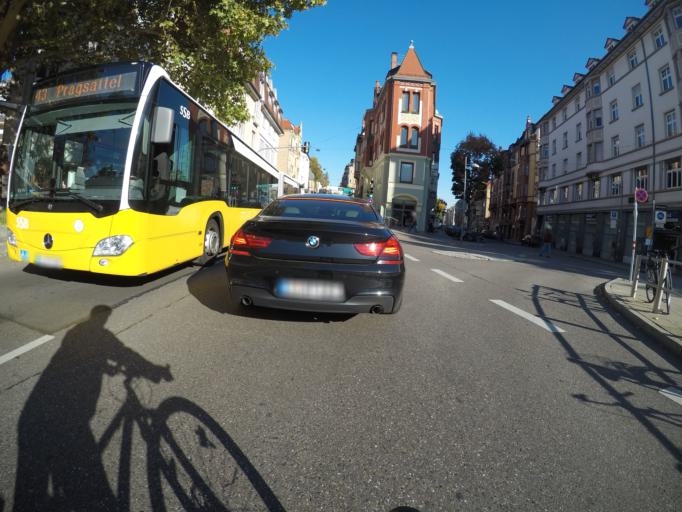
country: DE
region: Baden-Wuerttemberg
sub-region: Regierungsbezirk Stuttgart
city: Stuttgart
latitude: 48.7647
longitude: 9.1681
